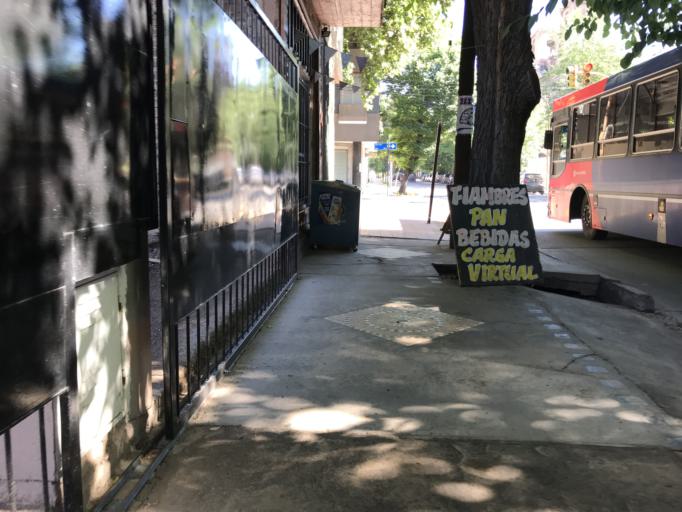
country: AR
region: Mendoza
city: Mendoza
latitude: -32.8854
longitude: -68.8313
